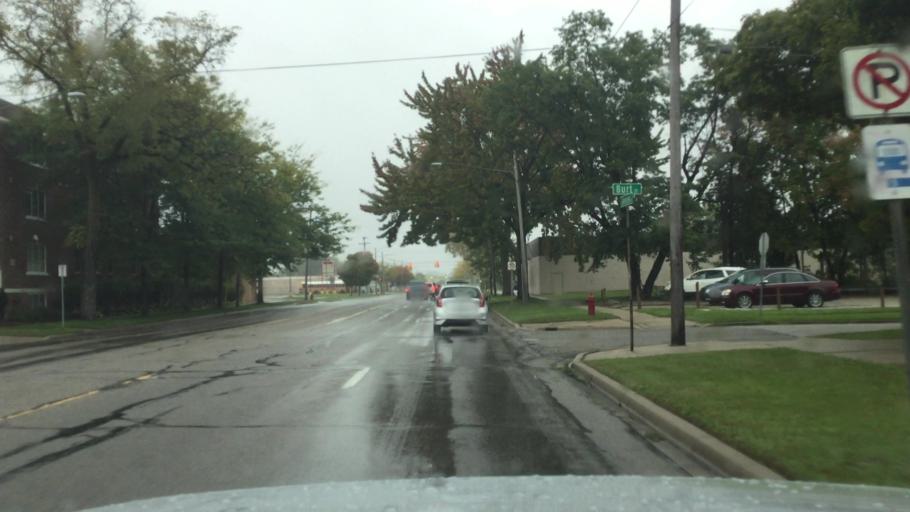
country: US
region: Michigan
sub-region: Saginaw County
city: Saginaw
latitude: 43.4248
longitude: -83.9283
